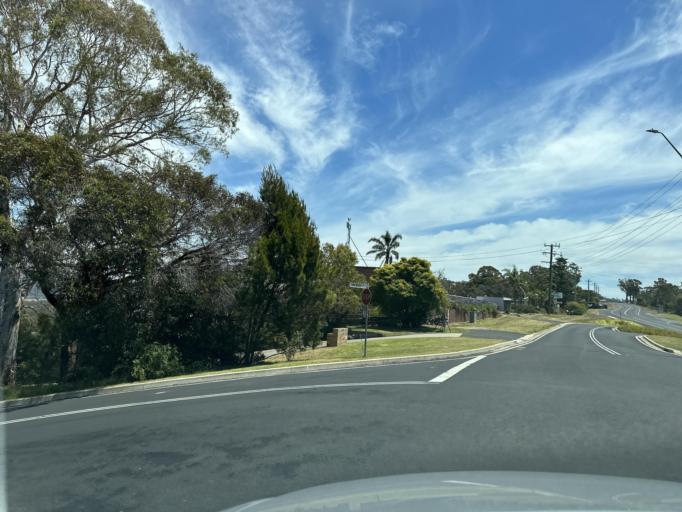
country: AU
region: New South Wales
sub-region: Bega Valley
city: Merimbula
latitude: -36.8894
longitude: 149.8974
